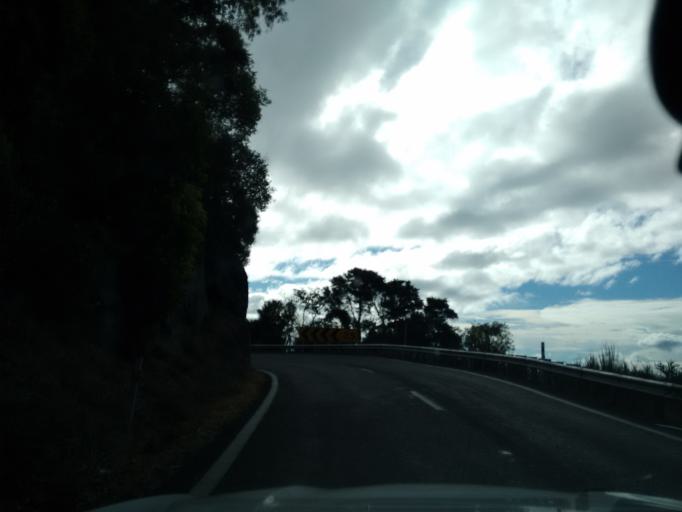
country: NZ
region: Waikato
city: Turangi
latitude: -38.8829
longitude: 175.9672
